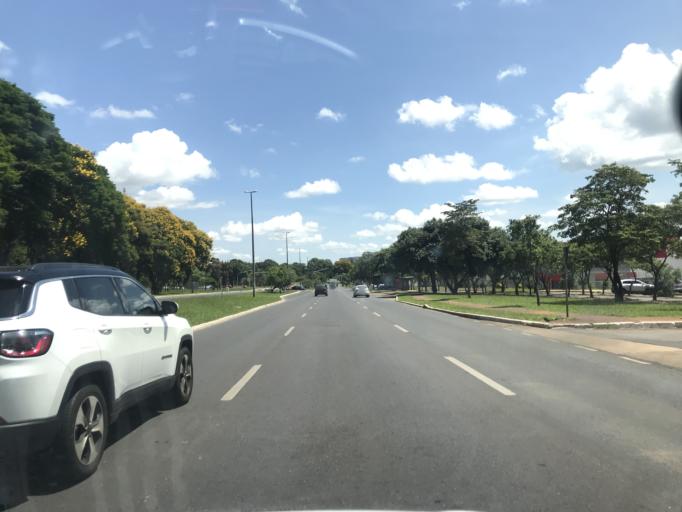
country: BR
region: Federal District
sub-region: Brasilia
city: Brasilia
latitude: -15.8077
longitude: -47.8820
